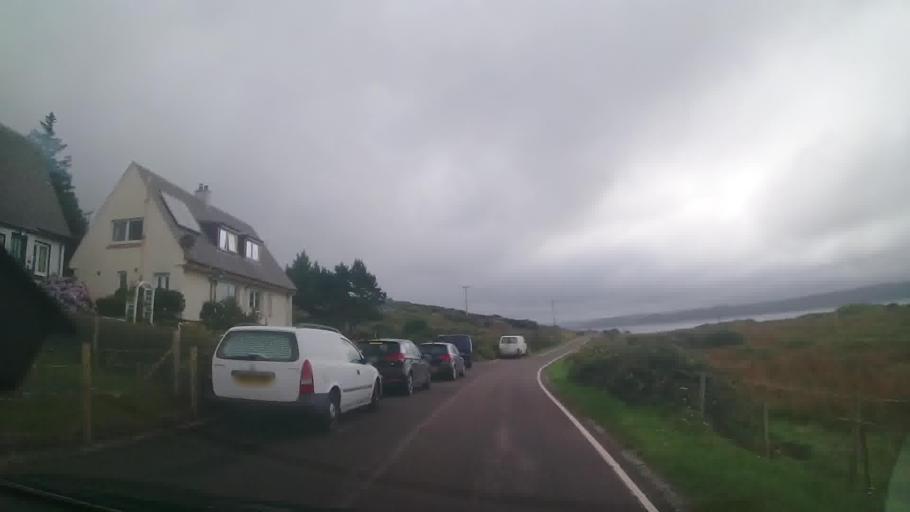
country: GB
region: Scotland
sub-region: Argyll and Bute
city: Isle Of Mull
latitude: 56.6934
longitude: -6.0956
